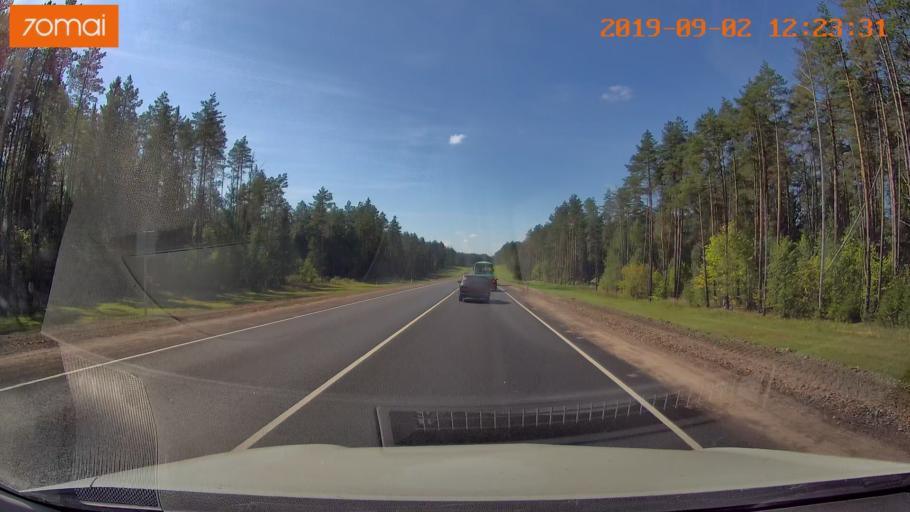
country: RU
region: Smolensk
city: Shumyachi
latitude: 53.8739
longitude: 32.6192
